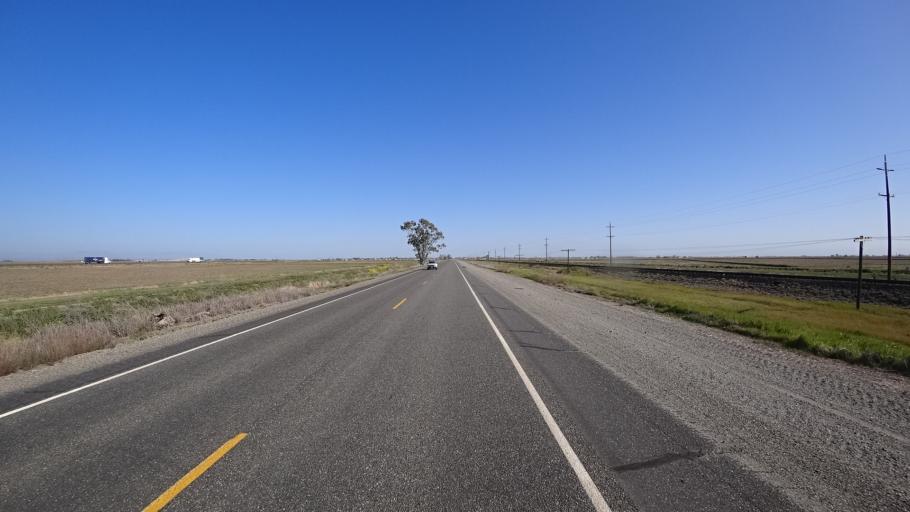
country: US
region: California
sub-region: Glenn County
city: Willows
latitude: 39.4740
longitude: -122.1930
